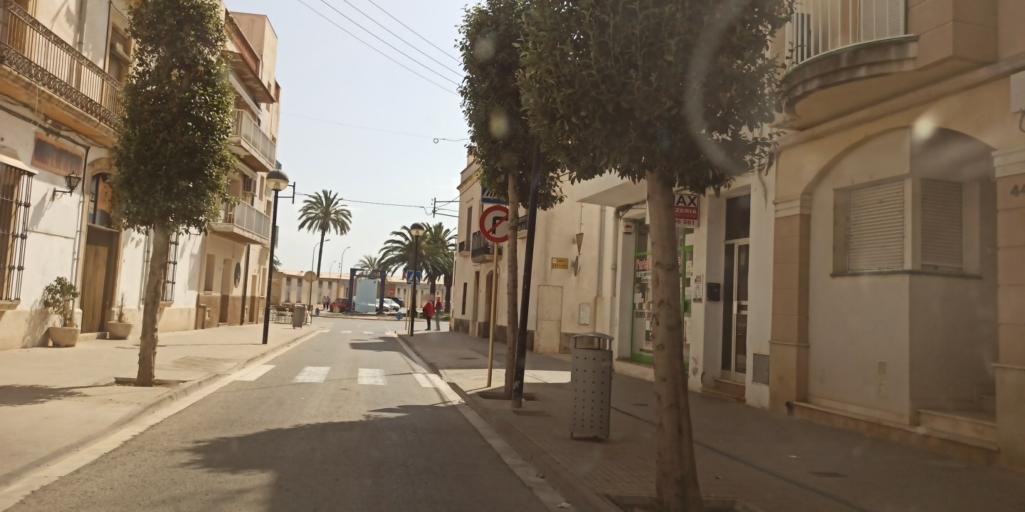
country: ES
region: Catalonia
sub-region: Provincia de Tarragona
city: Sant Carles de la Rapita
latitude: 40.6194
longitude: 0.5952
